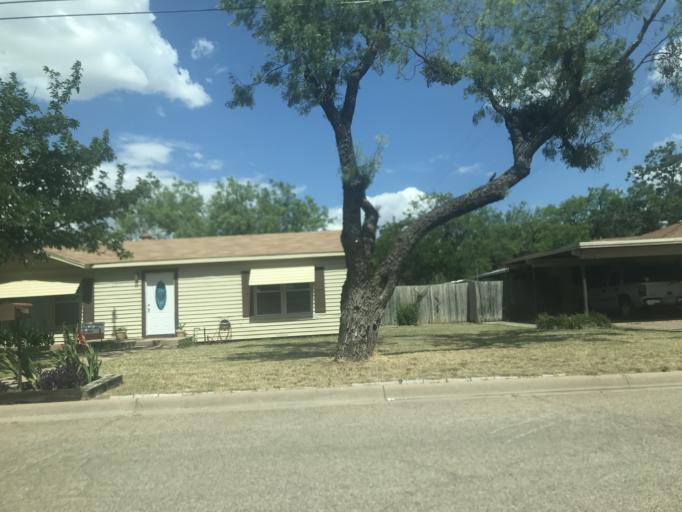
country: US
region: Texas
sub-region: Taylor County
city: Abilene
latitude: 32.4218
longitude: -99.7527
